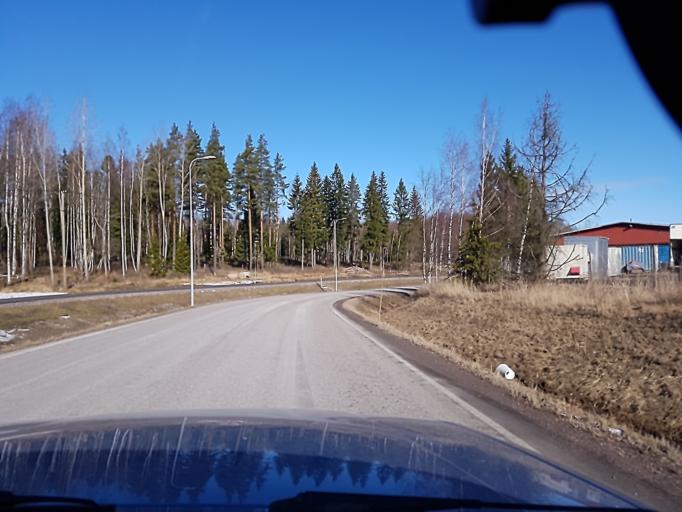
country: FI
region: Uusimaa
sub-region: Helsinki
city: Kilo
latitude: 60.2934
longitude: 24.8418
